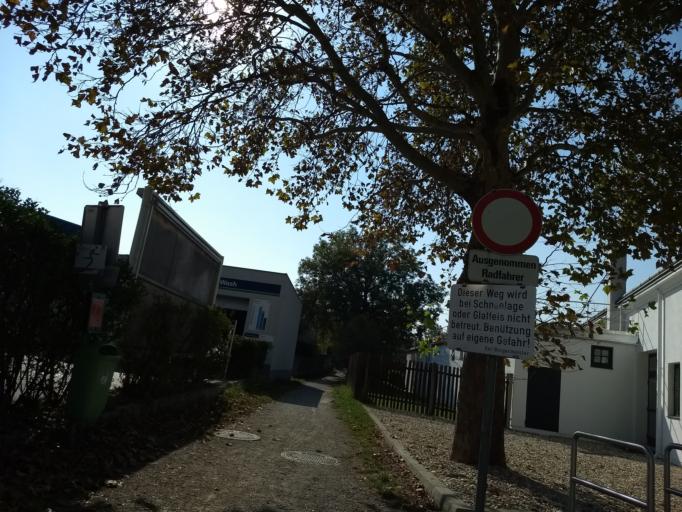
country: AT
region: Lower Austria
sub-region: Politischer Bezirk Modling
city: Perchtoldsdorf
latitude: 48.1158
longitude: 16.2717
